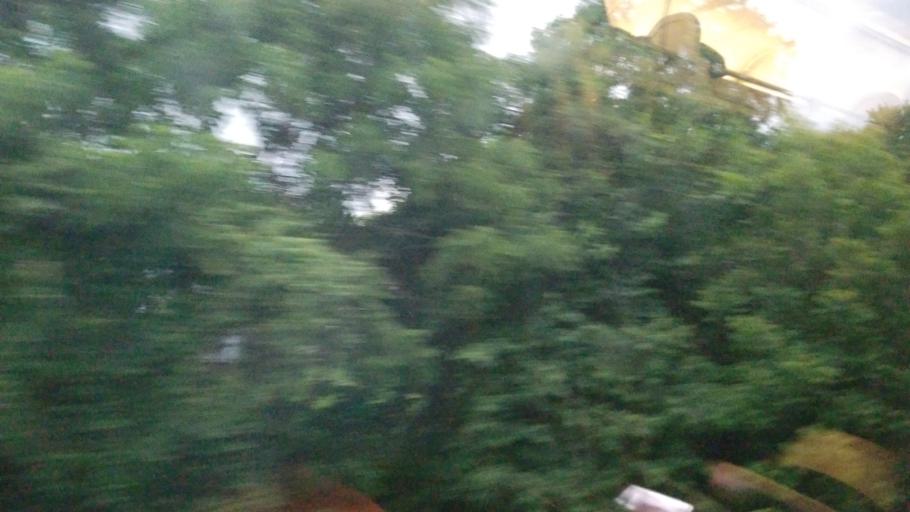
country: US
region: Virginia
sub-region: Orange County
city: Orange
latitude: 38.2510
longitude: -78.1096
